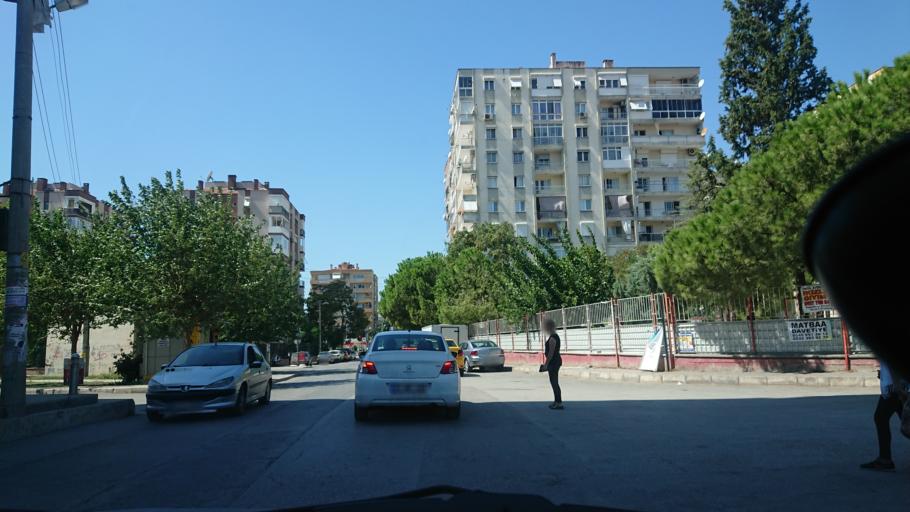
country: TR
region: Izmir
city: Karsiyaka
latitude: 38.4800
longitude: 27.1166
